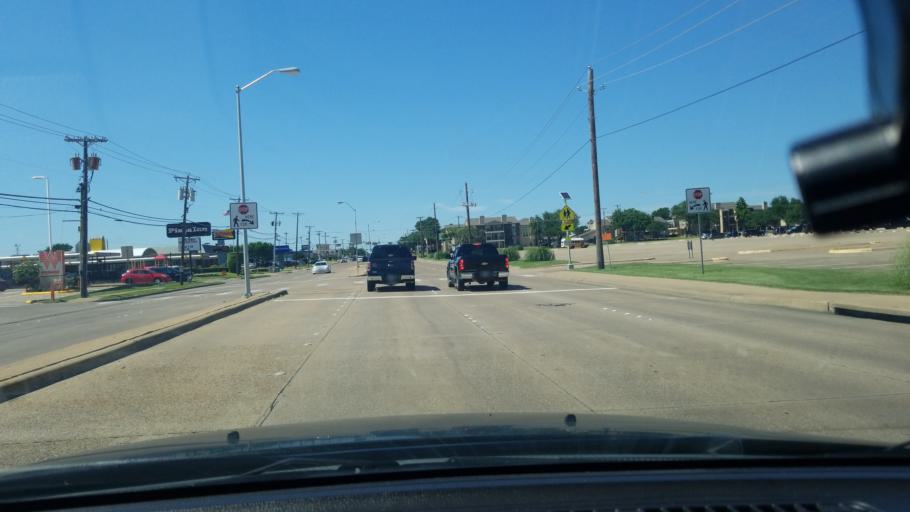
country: US
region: Texas
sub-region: Dallas County
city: Mesquite
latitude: 32.8063
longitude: -96.6112
